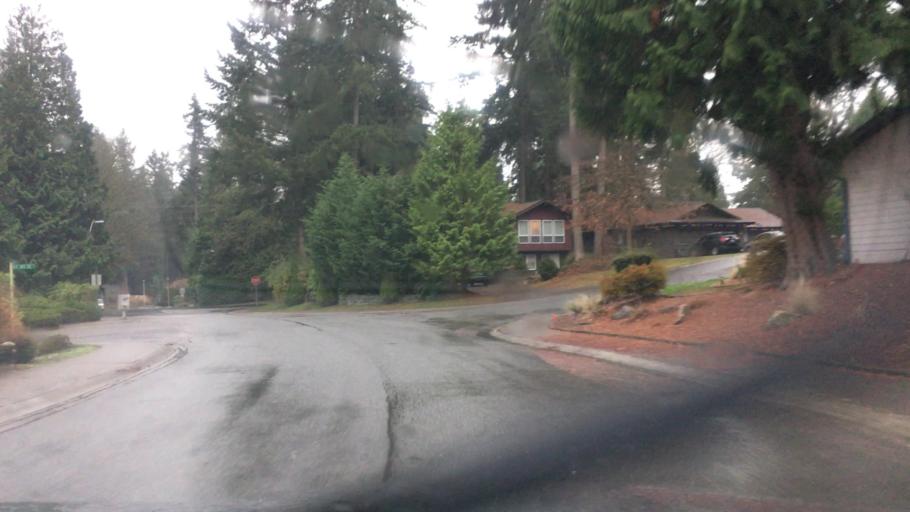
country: US
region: Washington
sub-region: King County
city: Kingsgate
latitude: 47.7339
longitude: -122.1981
